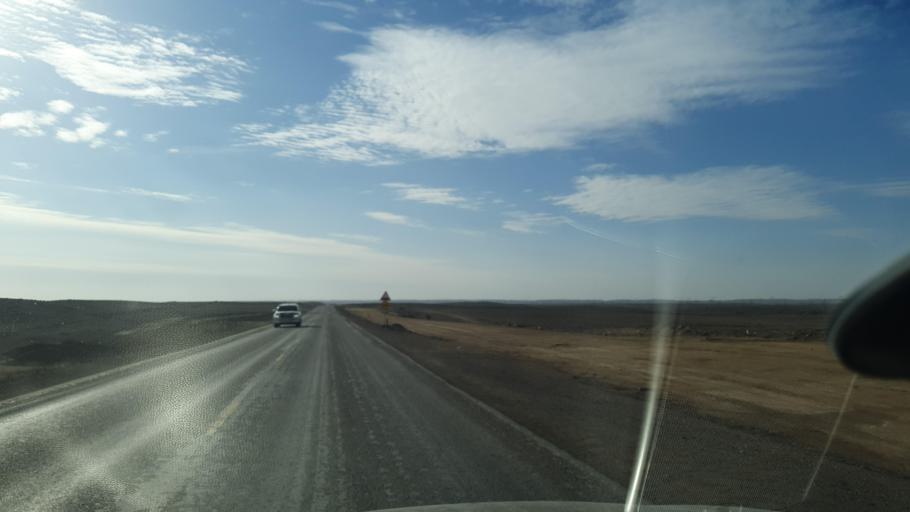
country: KZ
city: Priozersk
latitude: 45.8819
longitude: 73.4889
